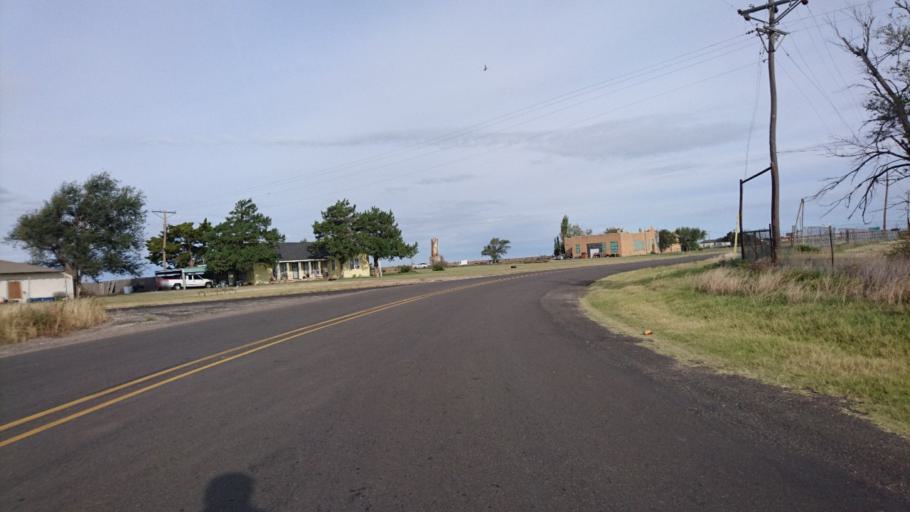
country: US
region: Texas
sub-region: Armstrong County
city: Claude
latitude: 35.2077
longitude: -101.3822
